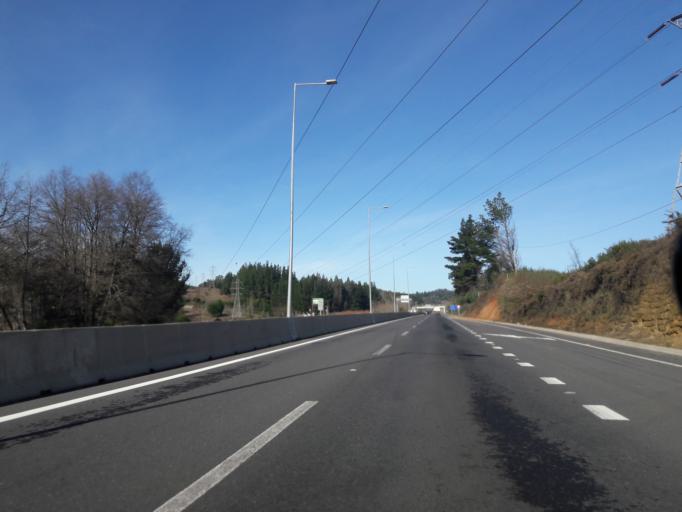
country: CL
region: Biobio
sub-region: Provincia de Concepcion
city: Chiguayante
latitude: -36.9113
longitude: -72.7777
